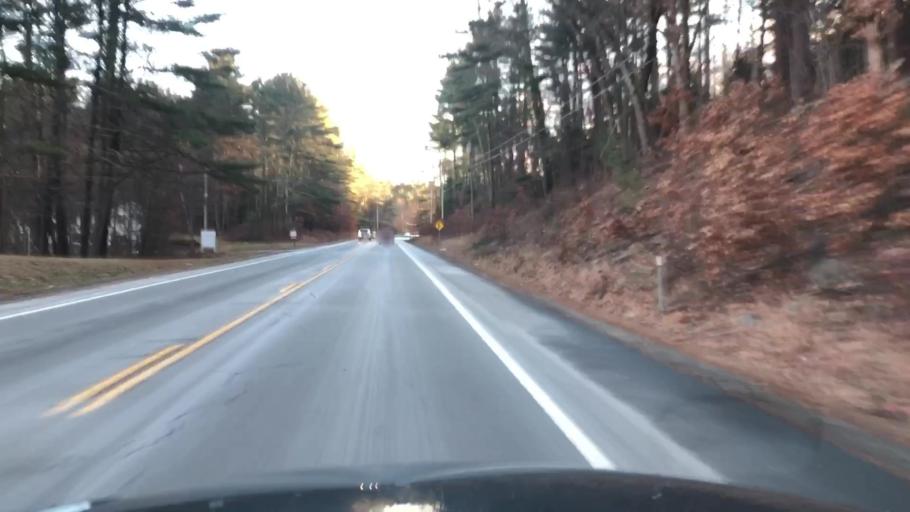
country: US
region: New Hampshire
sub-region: Hillsborough County
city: Brookline
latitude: 42.7192
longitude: -71.6625
